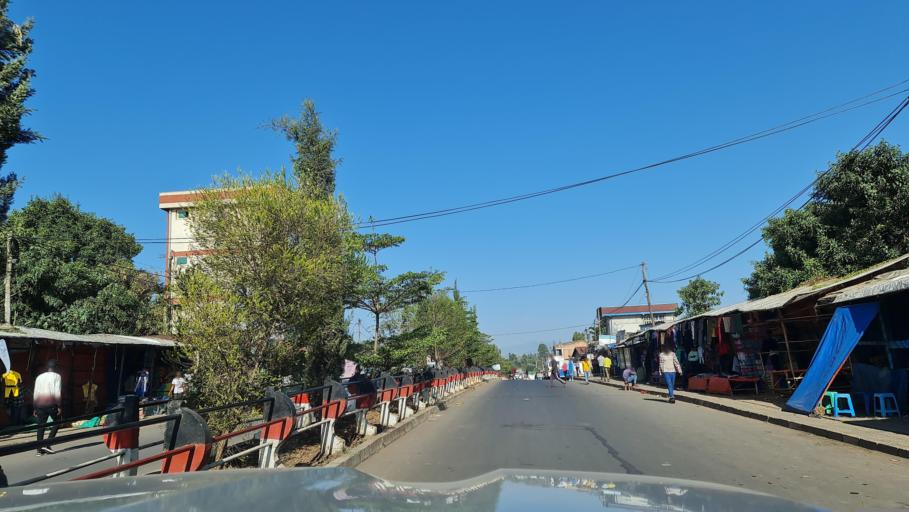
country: ET
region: Oromiya
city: Waliso
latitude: 8.5410
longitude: 37.9726
